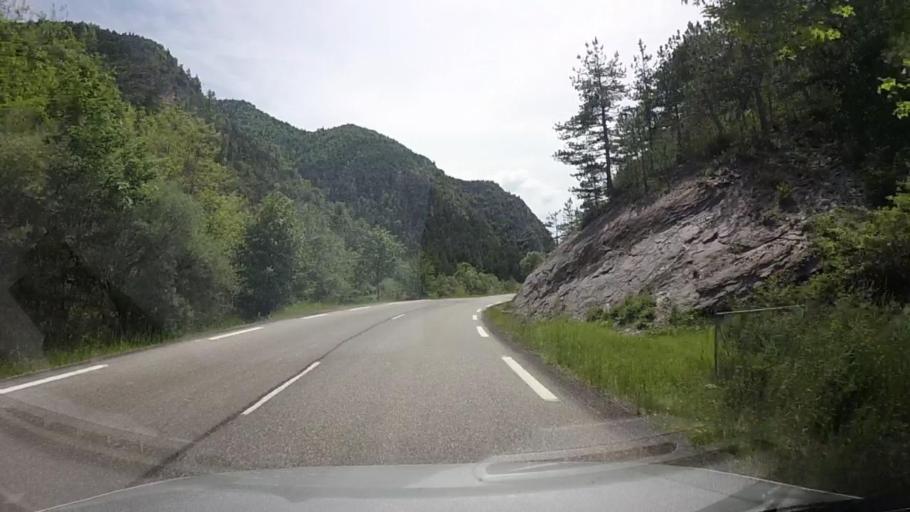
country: FR
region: Provence-Alpes-Cote d'Azur
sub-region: Departement des Alpes-de-Haute-Provence
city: Le Brusquet
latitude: 44.2020
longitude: 6.3714
